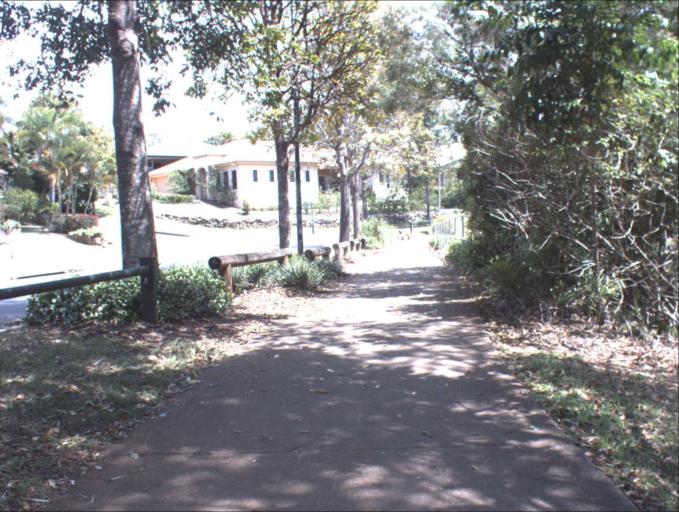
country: AU
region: Queensland
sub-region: Logan
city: Woodridge
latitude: -27.6107
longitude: 153.1043
